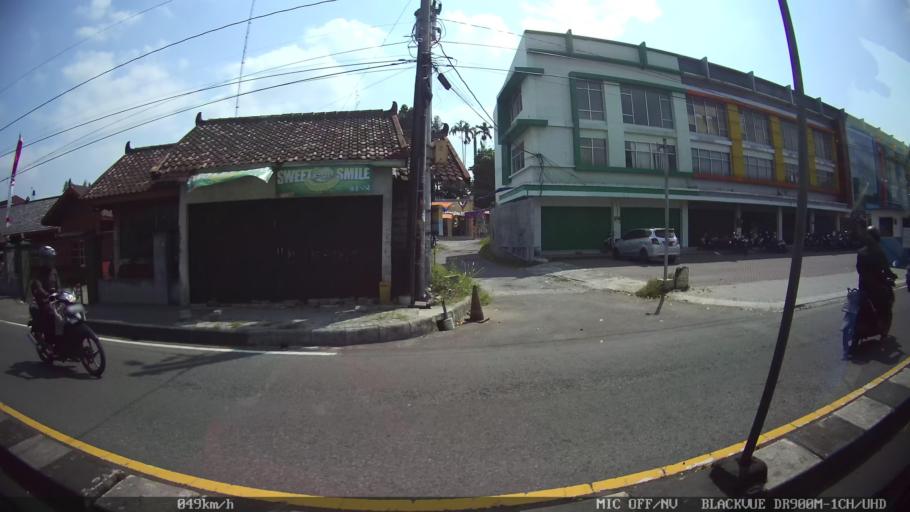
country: ID
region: Daerah Istimewa Yogyakarta
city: Melati
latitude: -7.7462
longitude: 110.3546
